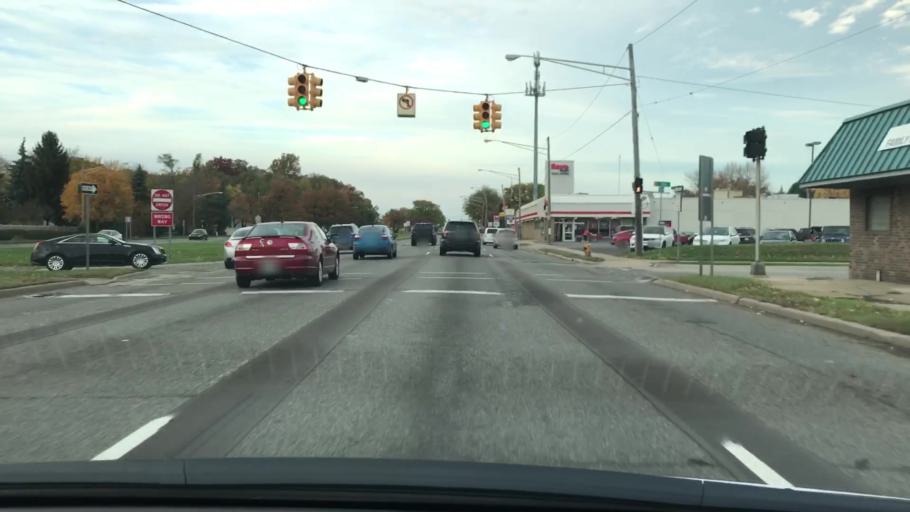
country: US
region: Michigan
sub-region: Wayne County
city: Inkster
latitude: 42.2883
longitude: -83.2709
